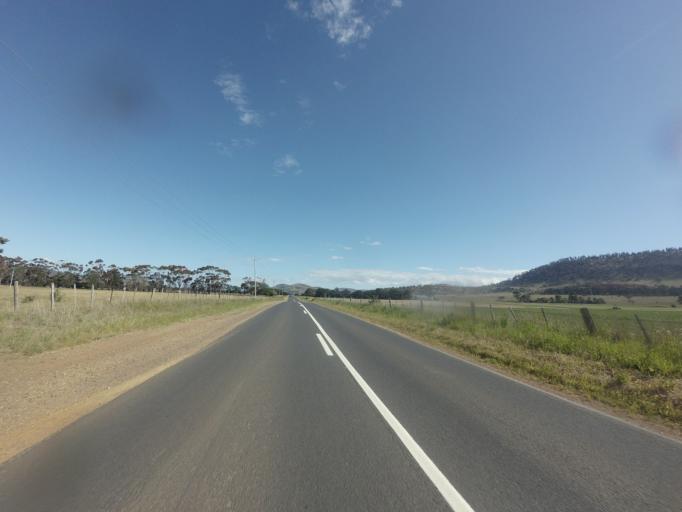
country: AU
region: Tasmania
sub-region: Clarence
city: Cambridge
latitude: -42.7023
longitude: 147.4295
